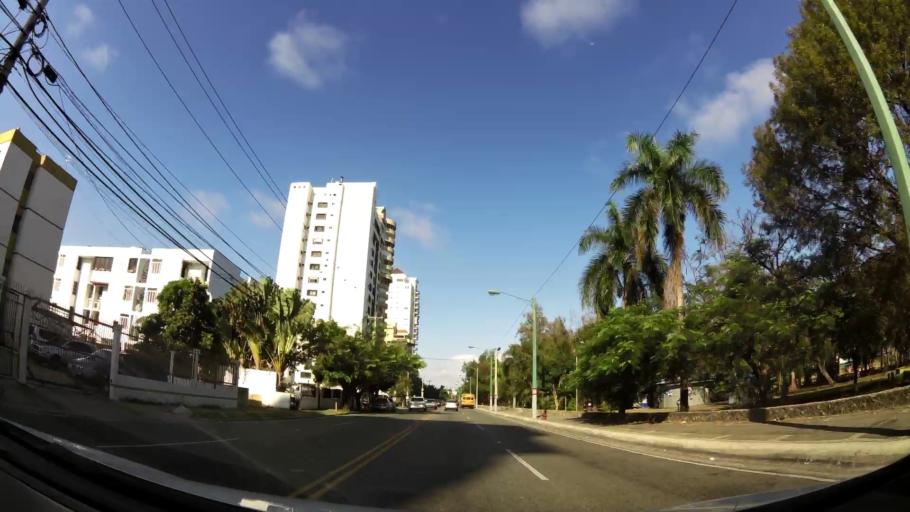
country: DO
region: Nacional
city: Bella Vista
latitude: 18.4508
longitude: -69.9397
